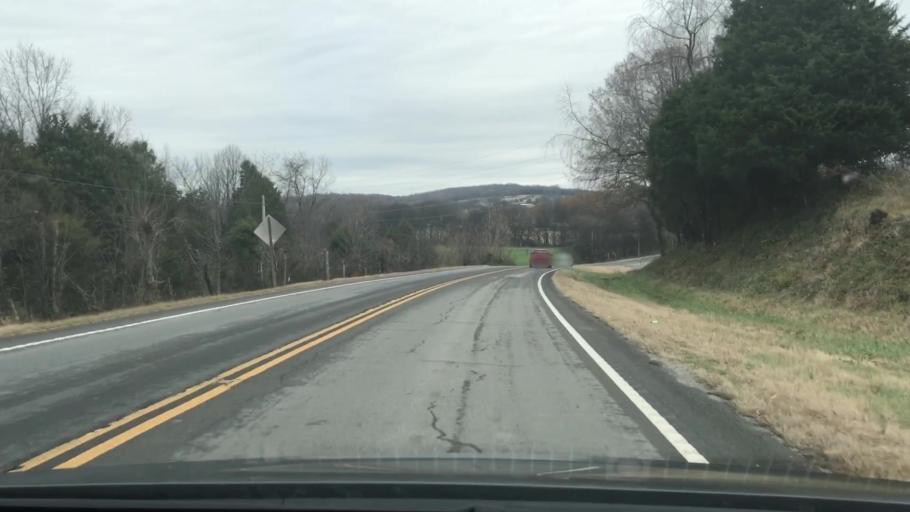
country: US
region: Tennessee
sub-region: Trousdale County
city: Hartsville
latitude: 36.3900
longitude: -86.2581
